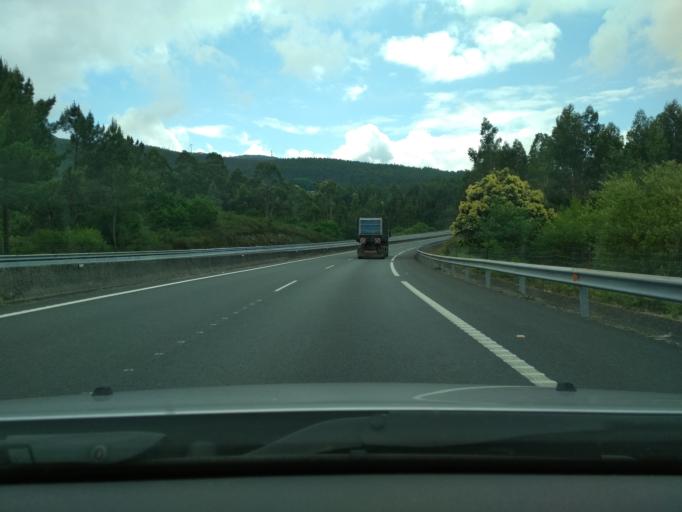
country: ES
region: Galicia
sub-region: Provincia da Coruna
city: Padron
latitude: 42.7780
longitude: -8.6421
